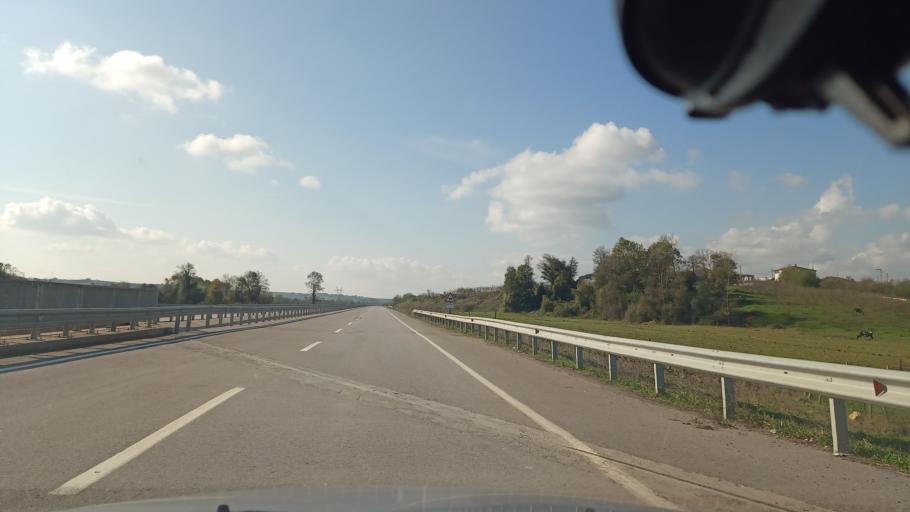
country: TR
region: Sakarya
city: Kaynarca
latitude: 41.0848
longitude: 30.4198
